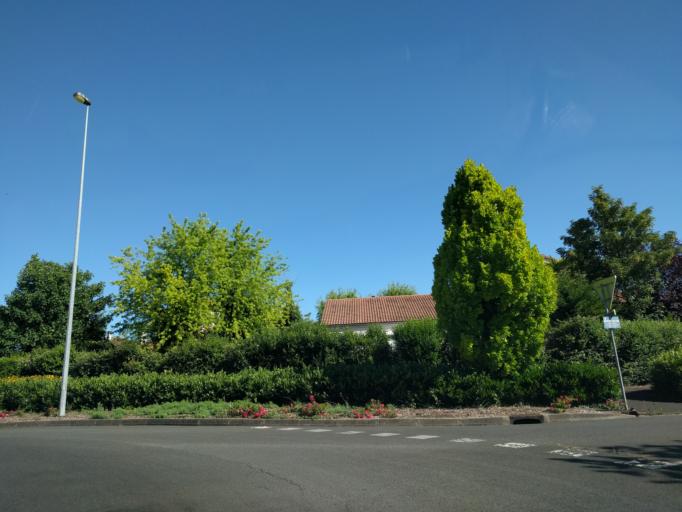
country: FR
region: Poitou-Charentes
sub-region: Departement des Deux-Sevres
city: Niort
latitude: 46.3408
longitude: -0.4387
